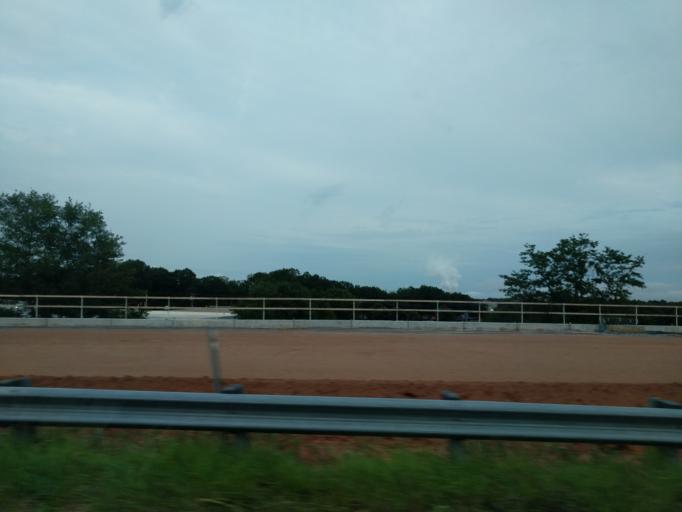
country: US
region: South Carolina
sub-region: Greenville County
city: Mauldin
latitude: 34.8304
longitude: -82.2943
